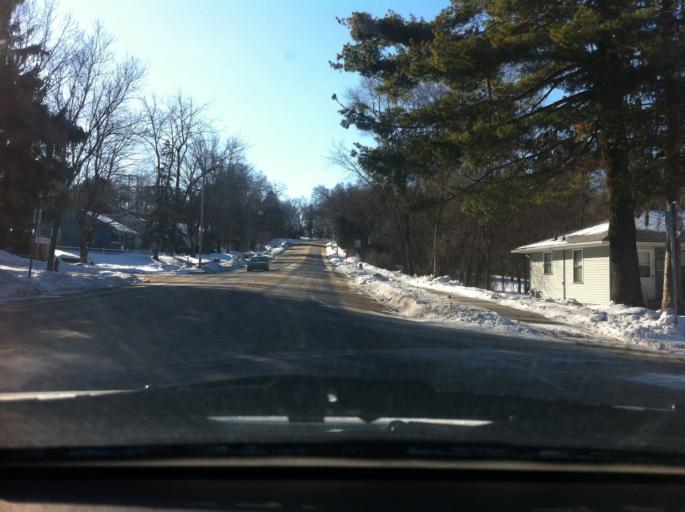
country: US
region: Wisconsin
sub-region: Dane County
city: Shorewood Hills
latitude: 43.0713
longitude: -89.4782
